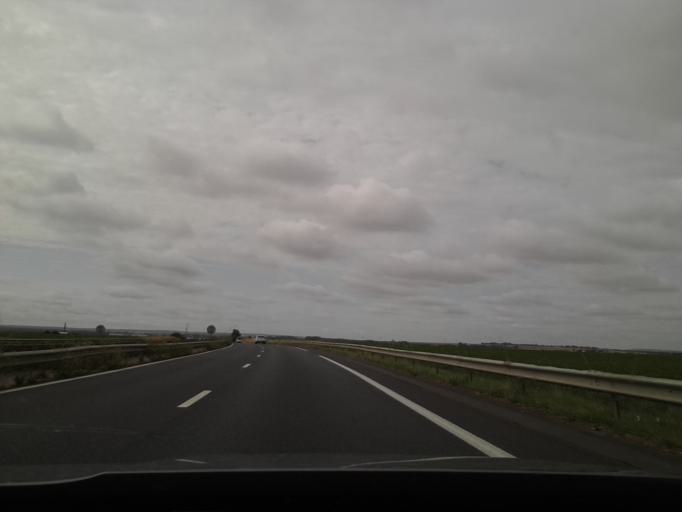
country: FR
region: Lower Normandy
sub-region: Departement du Calvados
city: Bretteville-sur-Odon
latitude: 49.1731
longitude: -0.4299
